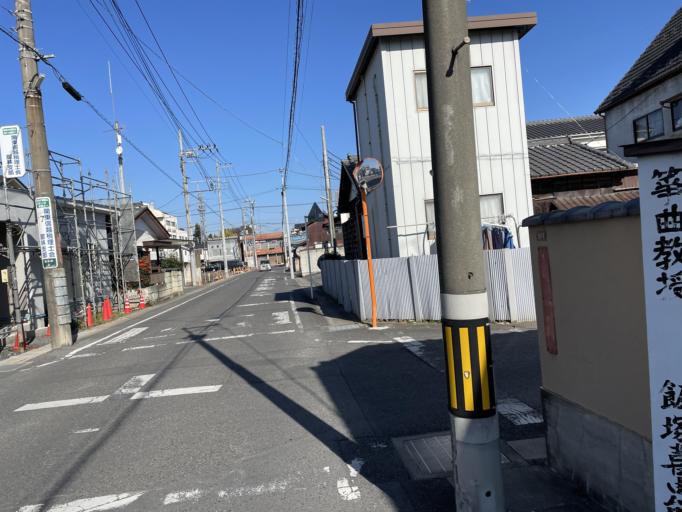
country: JP
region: Gunma
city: Tatebayashi
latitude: 36.2507
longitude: 139.5301
